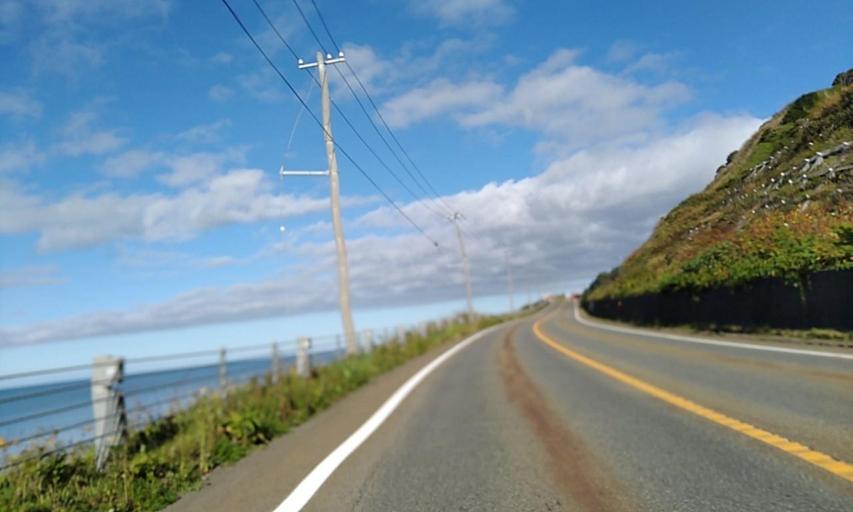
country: JP
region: Hokkaido
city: Shizunai-furukawacho
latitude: 42.2100
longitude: 142.6472
